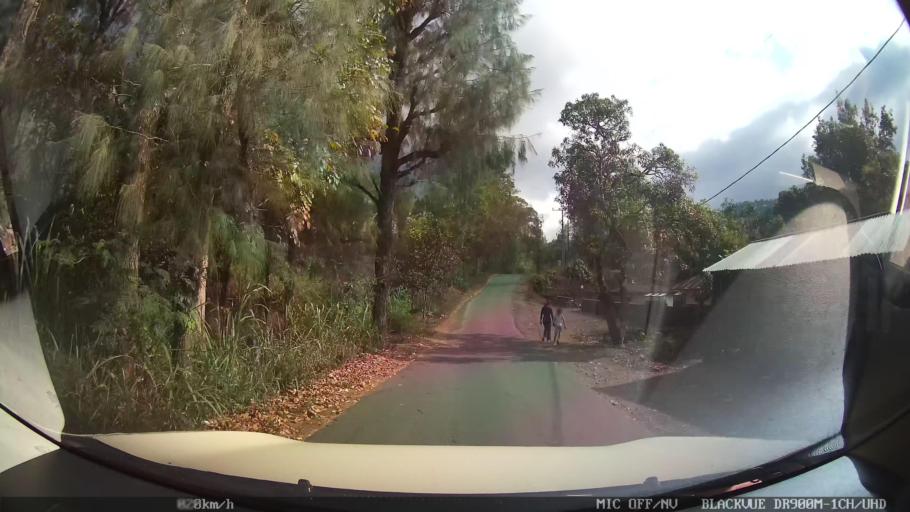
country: ID
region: Bali
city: Banjar Kedisan
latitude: -8.2314
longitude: 115.3574
